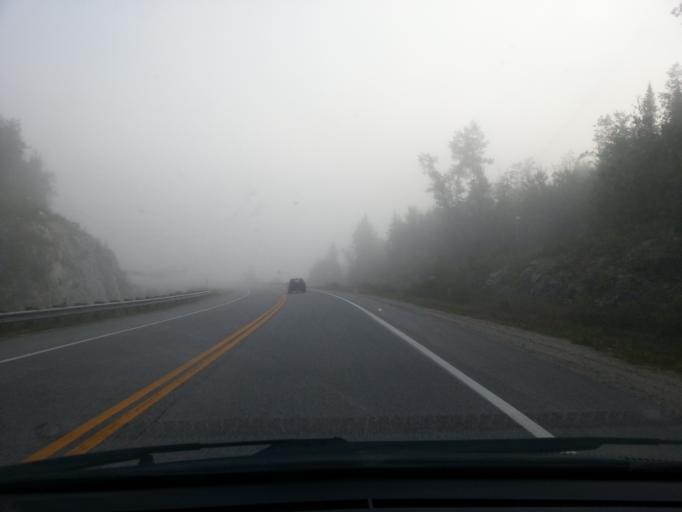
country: CA
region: Quebec
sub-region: Outaouais
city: Wakefield
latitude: 45.7292
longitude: -75.9085
